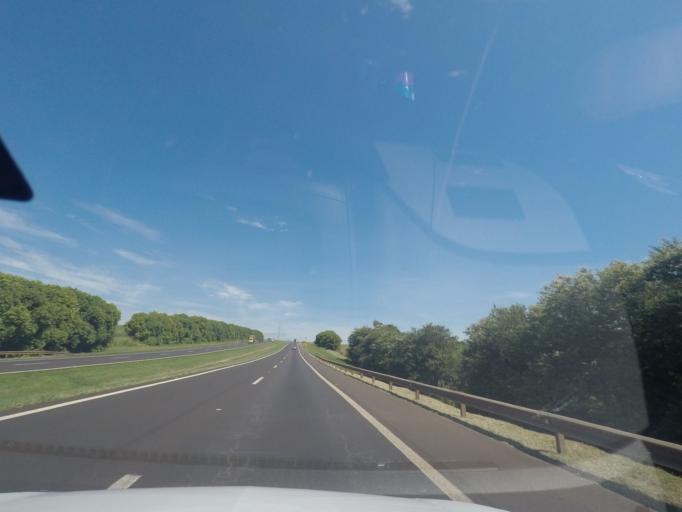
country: BR
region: Sao Paulo
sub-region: Araraquara
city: Araraquara
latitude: -21.8671
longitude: -48.1105
